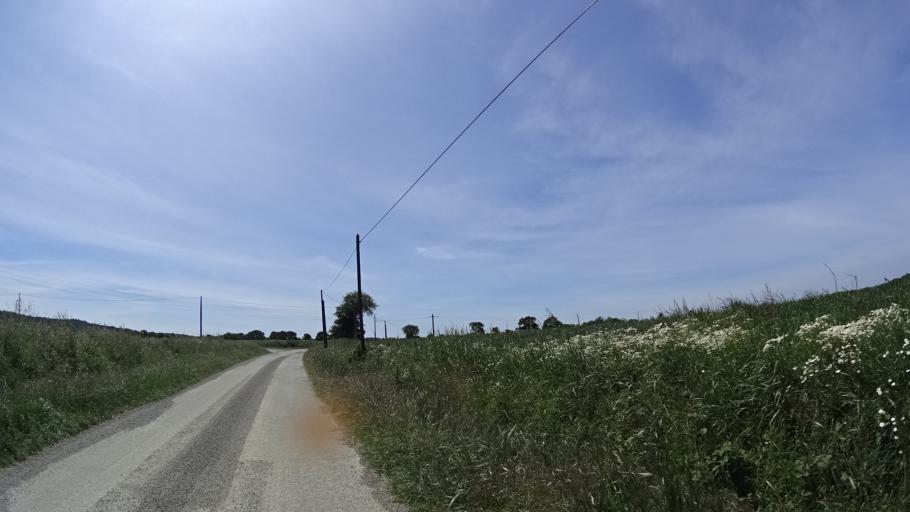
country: FR
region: Brittany
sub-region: Departement d'Ille-et-Vilaine
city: Iffendic
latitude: 48.1260
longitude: -2.0142
